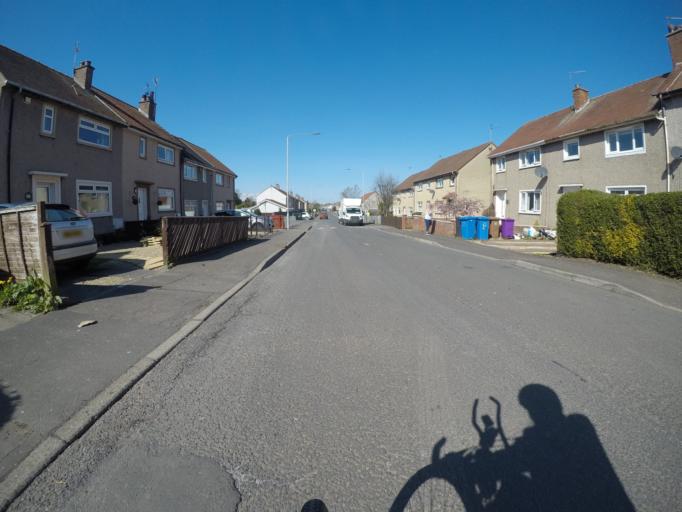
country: GB
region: Scotland
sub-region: North Ayrshire
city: Irvine
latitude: 55.6244
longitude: -4.6564
